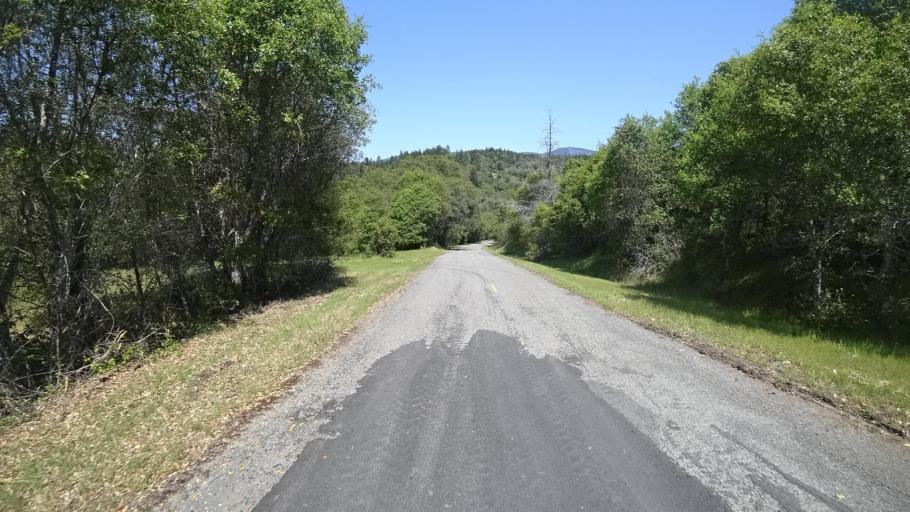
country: US
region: California
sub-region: Humboldt County
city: Redway
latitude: 40.2351
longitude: -123.6380
